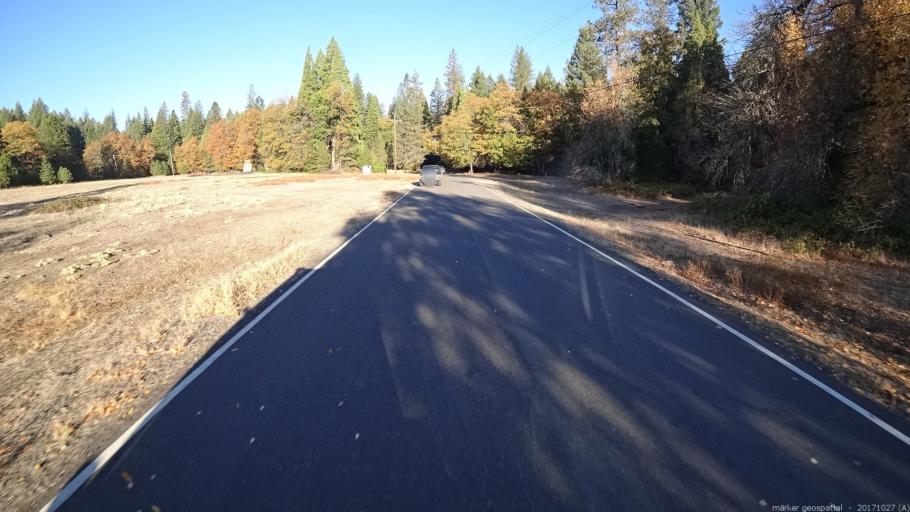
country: US
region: California
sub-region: Shasta County
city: Burney
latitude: 41.0021
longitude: -121.8899
